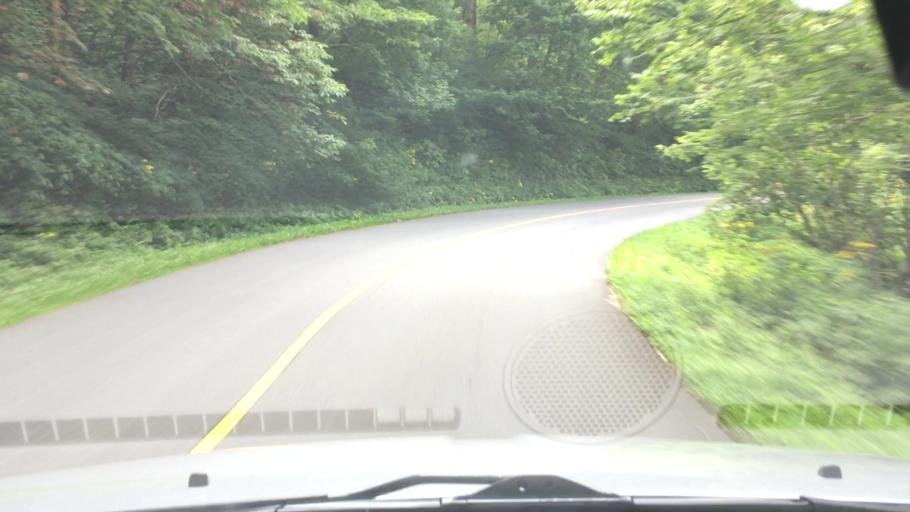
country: US
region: North Carolina
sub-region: Buncombe County
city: Swannanoa
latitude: 35.7012
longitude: -82.3925
